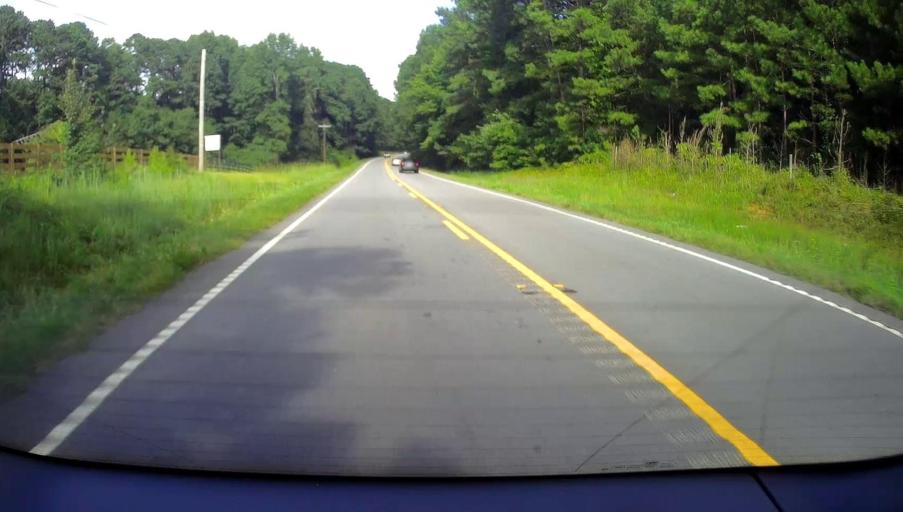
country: US
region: Georgia
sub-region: Meriwether County
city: Manchester
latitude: 32.9841
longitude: -84.5640
